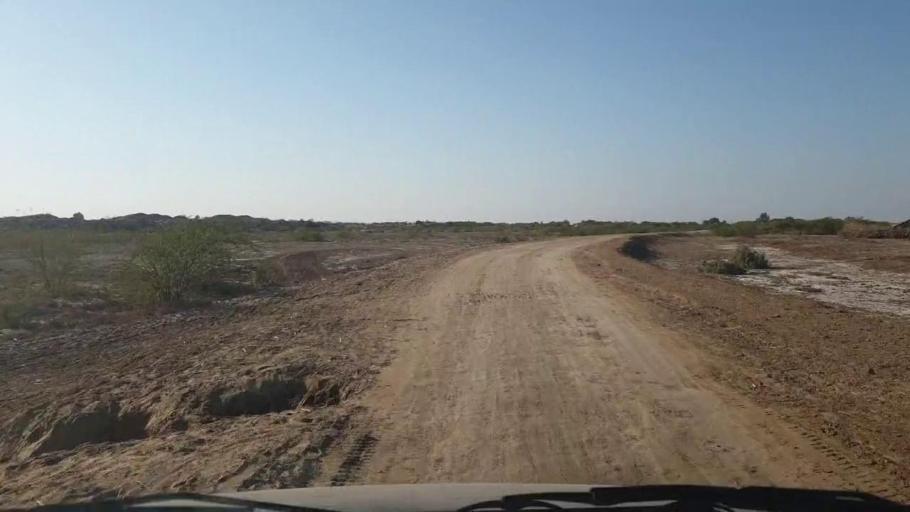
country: PK
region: Sindh
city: Samaro
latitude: 25.3606
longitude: 69.2948
